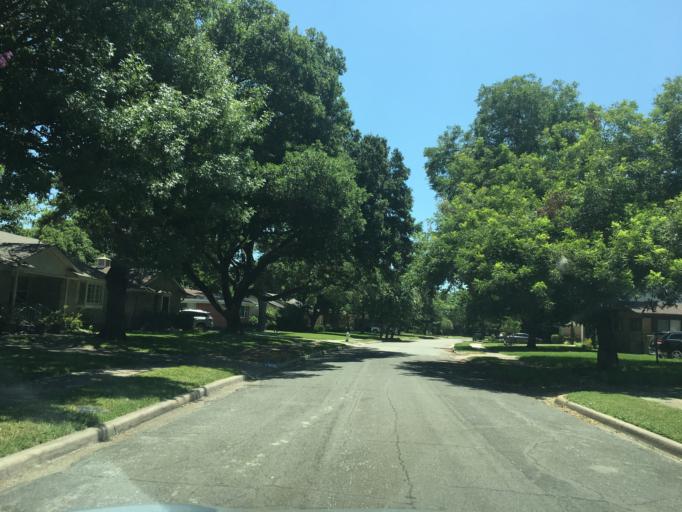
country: US
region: Texas
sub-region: Dallas County
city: Highland Park
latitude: 32.8534
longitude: -96.7401
